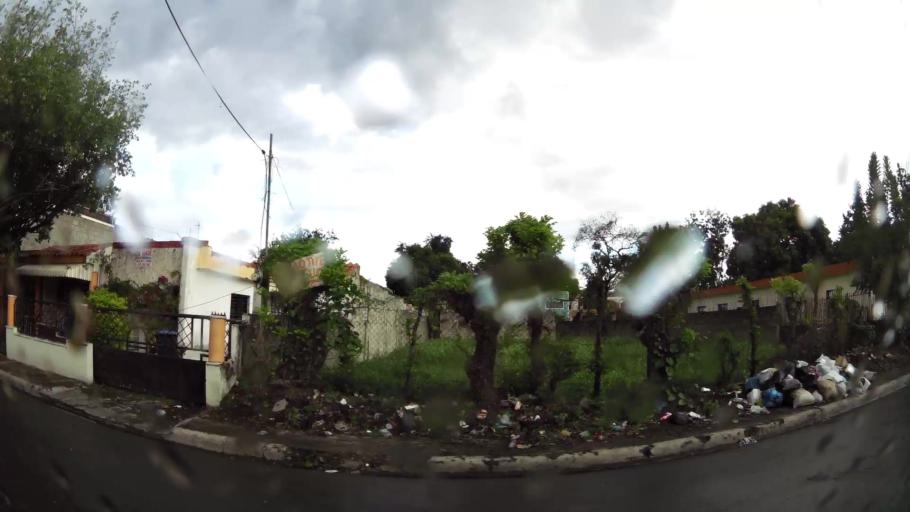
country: DO
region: Monsenor Nouel
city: Bonao
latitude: 18.9350
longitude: -70.4035
